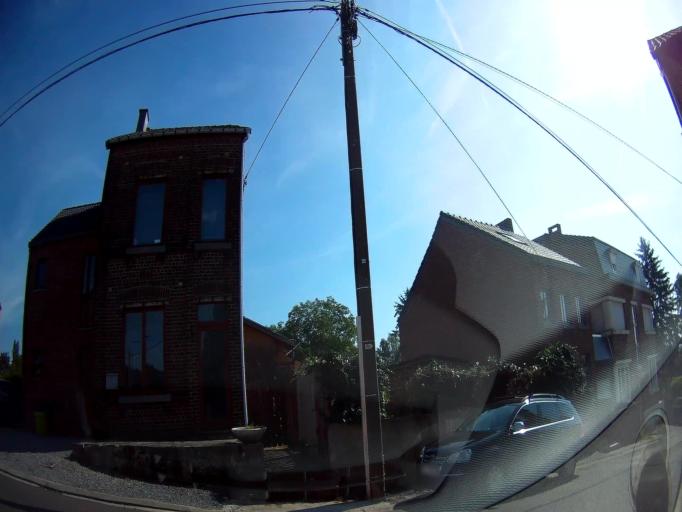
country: BE
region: Wallonia
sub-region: Province de Liege
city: Amay
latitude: 50.5507
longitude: 5.3132
